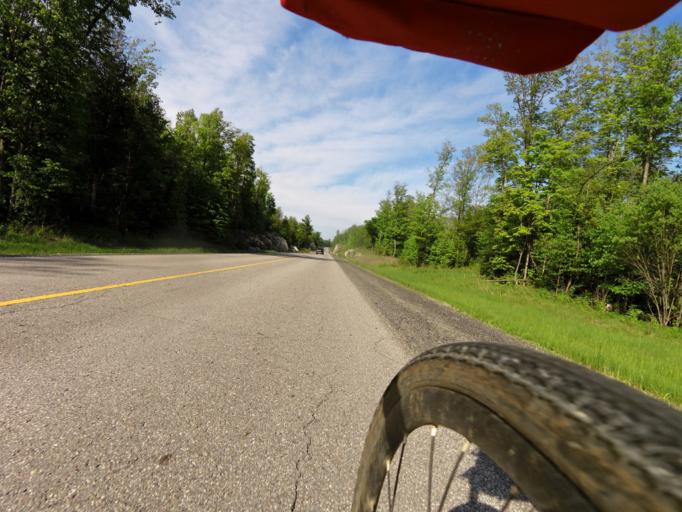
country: CA
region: Ontario
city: Arnprior
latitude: 45.1653
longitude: -76.5002
